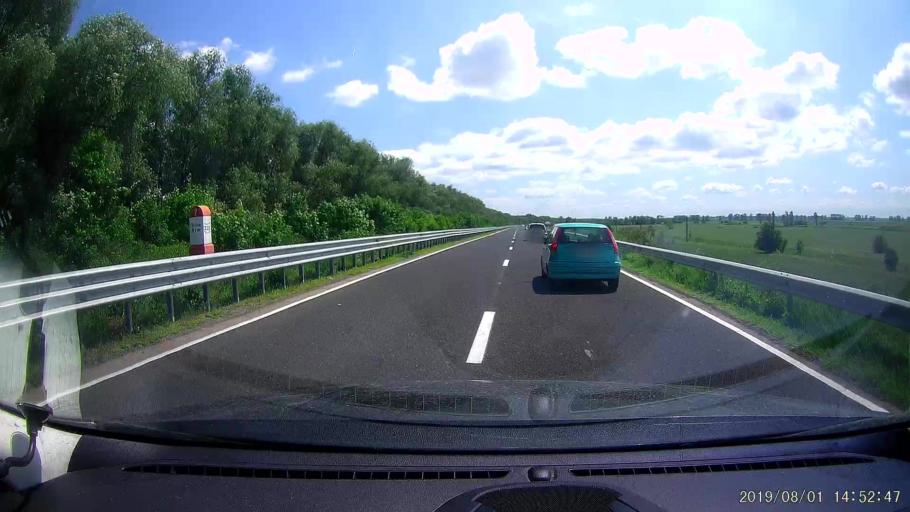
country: RO
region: Braila
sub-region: Comuna Vadeni
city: Vadeni
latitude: 45.3487
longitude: 28.0086
